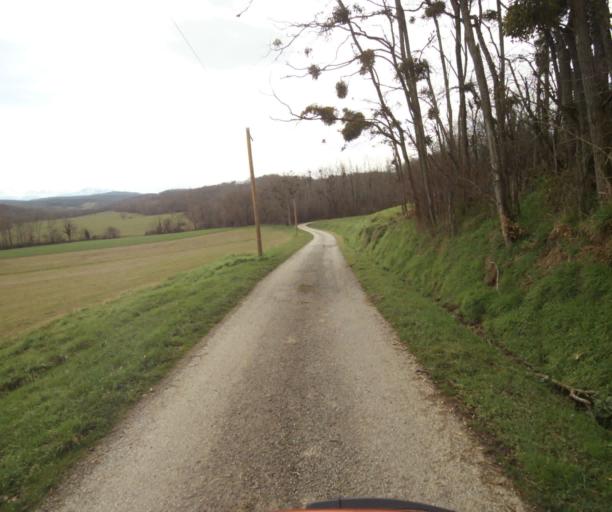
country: FR
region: Midi-Pyrenees
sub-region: Departement de l'Ariege
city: Verniolle
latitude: 43.0774
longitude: 1.7092
